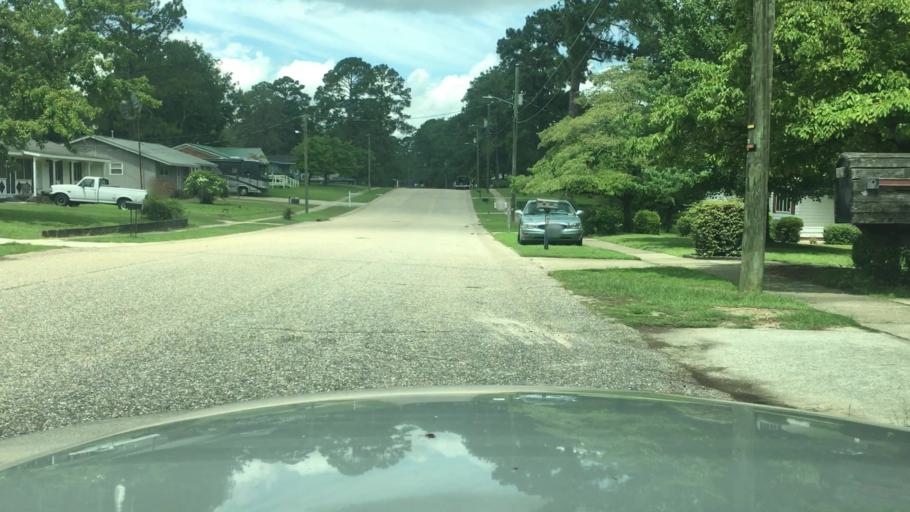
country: US
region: North Carolina
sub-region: Cumberland County
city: Fayetteville
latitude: 35.0498
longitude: -78.9539
